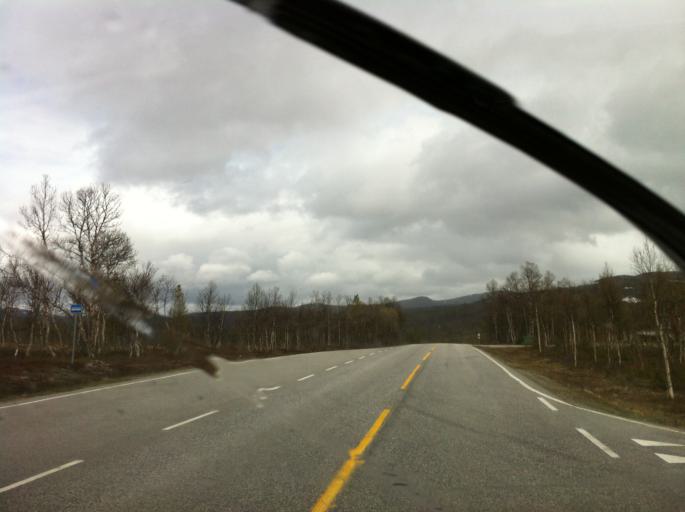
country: NO
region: Sor-Trondelag
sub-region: Roros
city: Roros
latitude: 62.5969
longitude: 11.7320
